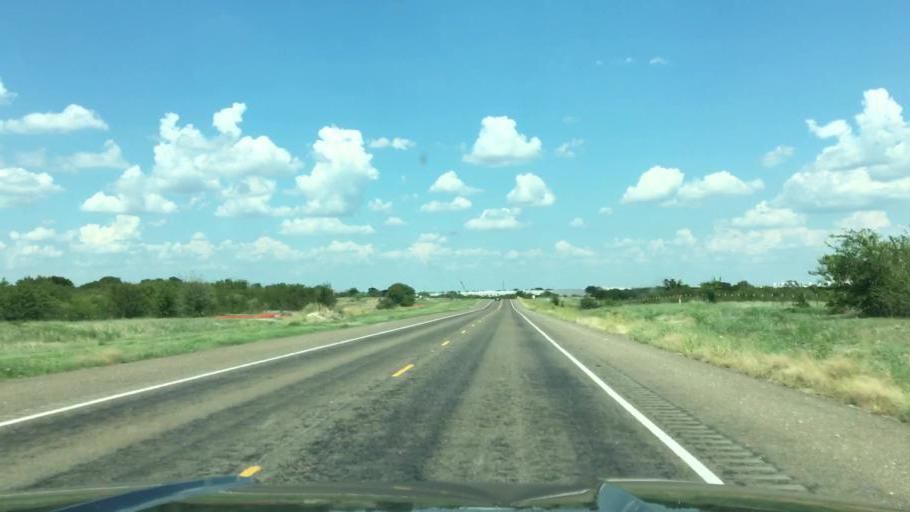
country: US
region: Texas
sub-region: Tarrant County
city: Haslet
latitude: 33.0120
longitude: -97.3378
